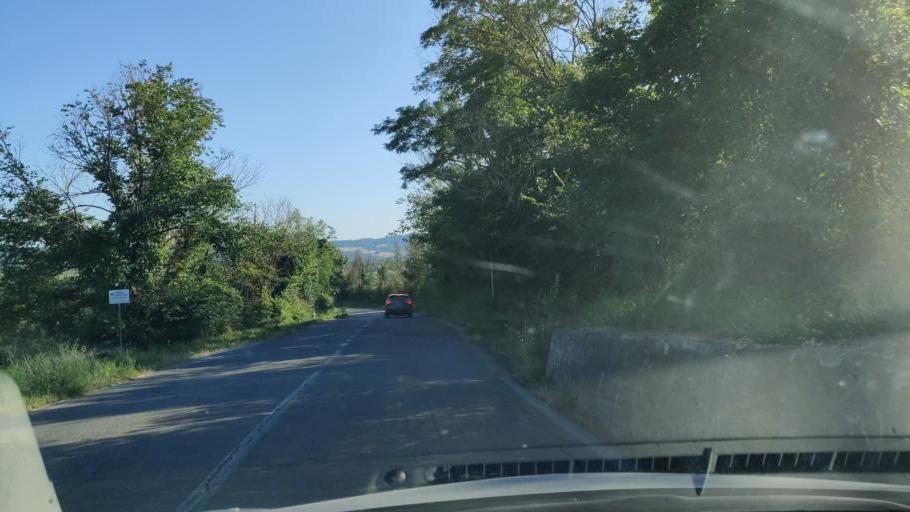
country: IT
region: Umbria
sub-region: Provincia di Terni
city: Penna in Teverina
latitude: 42.4868
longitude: 12.3700
